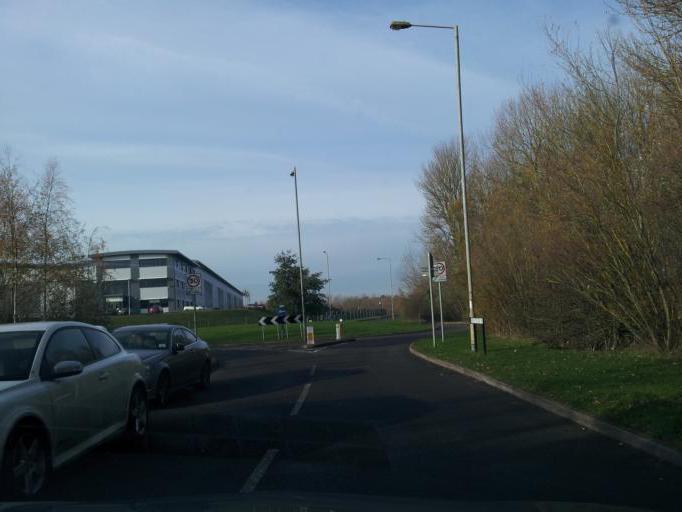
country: GB
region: England
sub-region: Northamptonshire
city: Hardingstone
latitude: 52.1947
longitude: -0.8840
